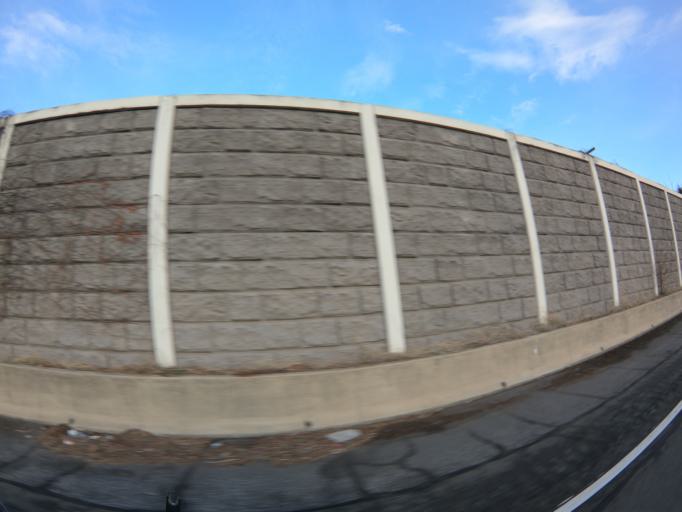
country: US
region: Maryland
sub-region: Howard County
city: Columbia
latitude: 39.2512
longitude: -76.8269
